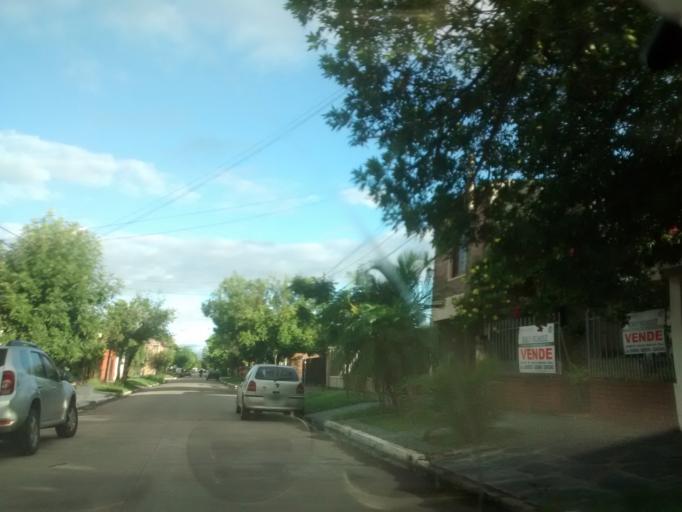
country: AR
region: Chaco
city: Resistencia
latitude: -27.4588
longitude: -58.9986
